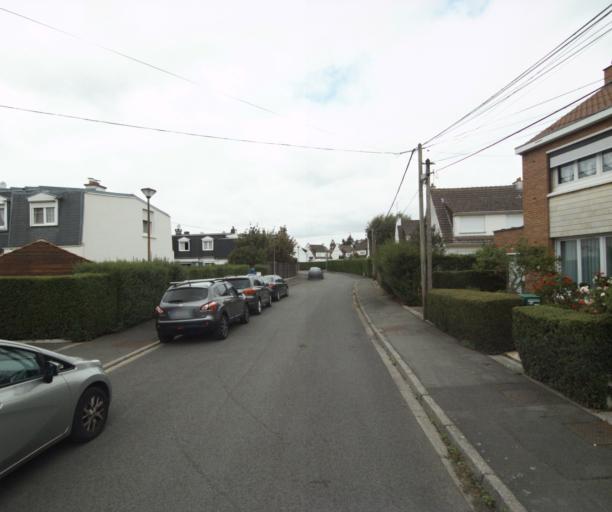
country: FR
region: Nord-Pas-de-Calais
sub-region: Departement du Nord
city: Leers
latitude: 50.6776
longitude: 3.2437
